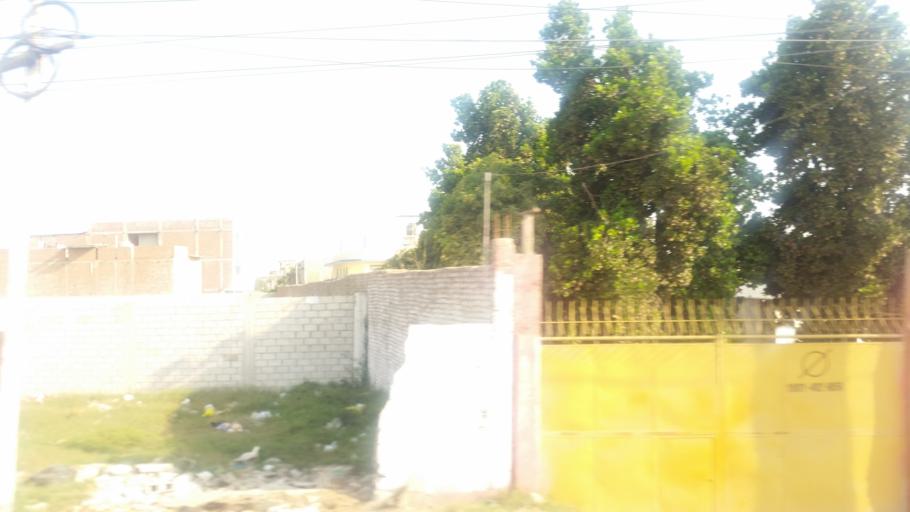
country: PE
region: La Libertad
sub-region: Chepen
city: Chepen
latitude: -7.2228
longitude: -79.4389
